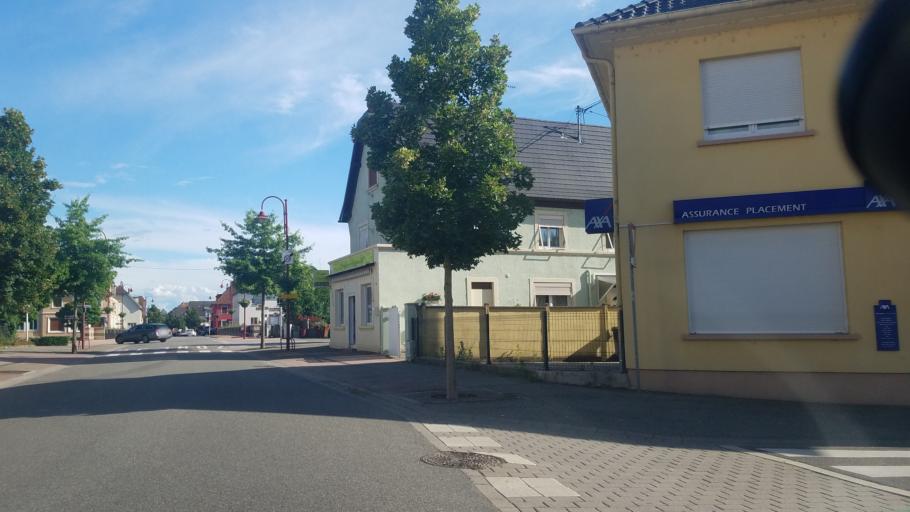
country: FR
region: Alsace
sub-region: Departement du Bas-Rhin
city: Drusenheim
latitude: 48.7623
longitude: 7.9512
